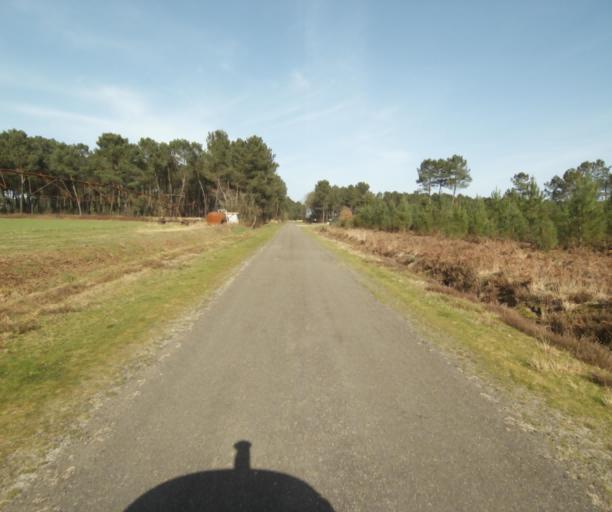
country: FR
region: Aquitaine
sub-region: Departement des Landes
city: Roquefort
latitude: 44.1717
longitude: -0.1958
